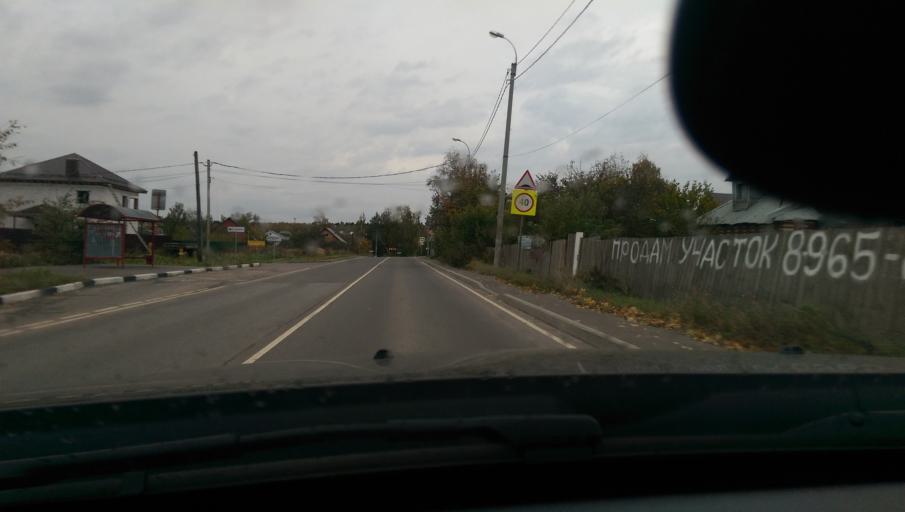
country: RU
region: Moskovskaya
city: Pirogovskiy
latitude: 56.0107
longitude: 37.7195
